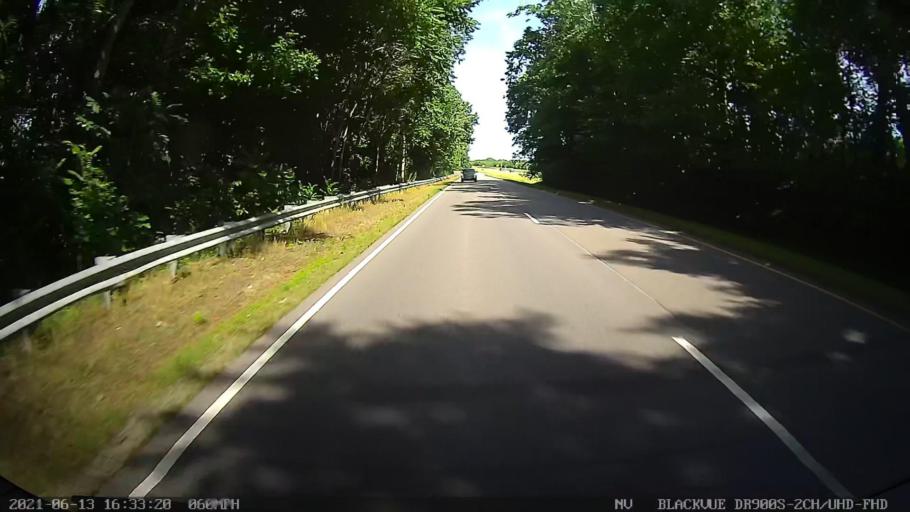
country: US
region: Virginia
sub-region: City of Hopewell
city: Hopewell
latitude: 37.2856
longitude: -77.2470
